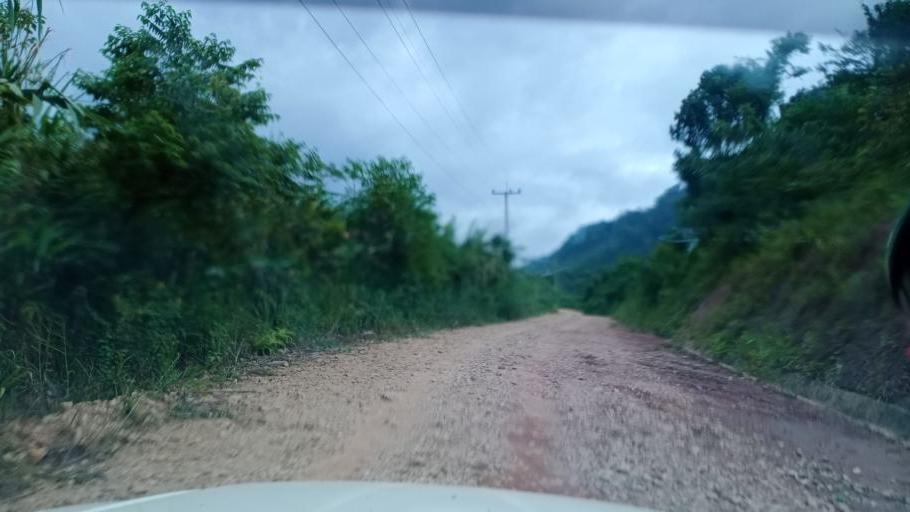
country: TH
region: Changwat Bueng Kan
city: Pak Khat
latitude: 18.7259
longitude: 103.2669
